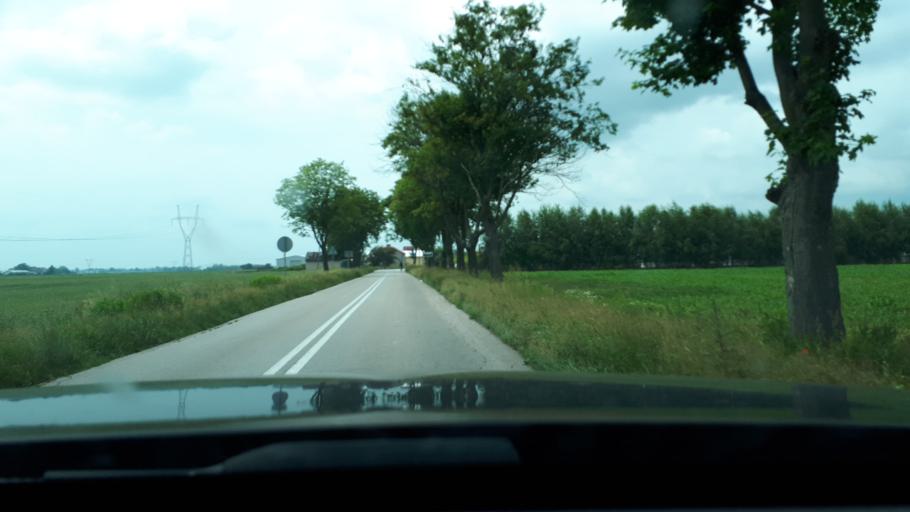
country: PL
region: Masovian Voivodeship
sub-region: Powiat warszawski zachodni
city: Jozefow
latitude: 52.2367
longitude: 20.6602
